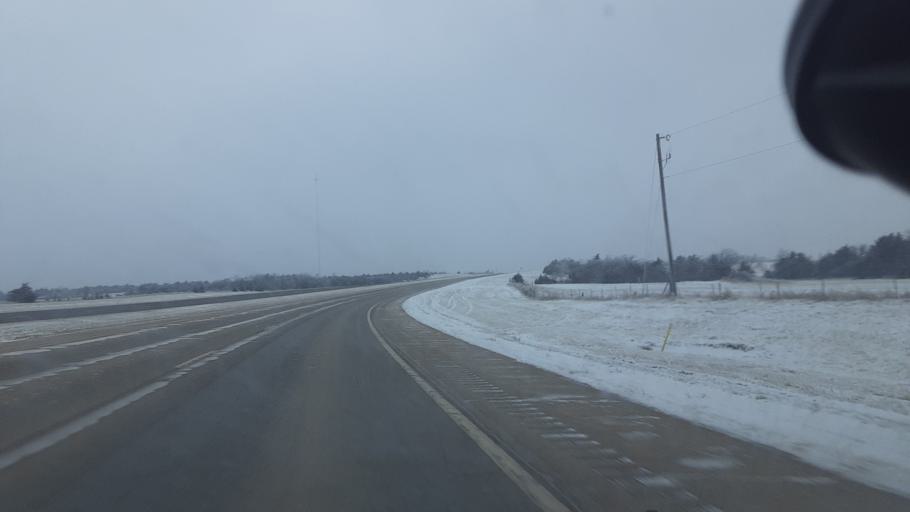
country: US
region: Oklahoma
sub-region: Logan County
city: Guthrie
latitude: 35.9052
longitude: -97.3386
